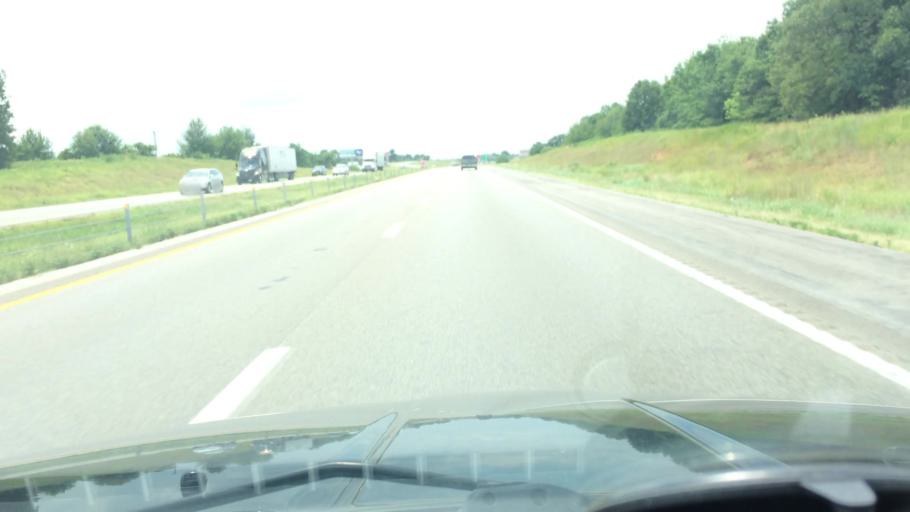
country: US
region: Missouri
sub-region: Greene County
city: Strafford
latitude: 37.2537
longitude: -93.1732
